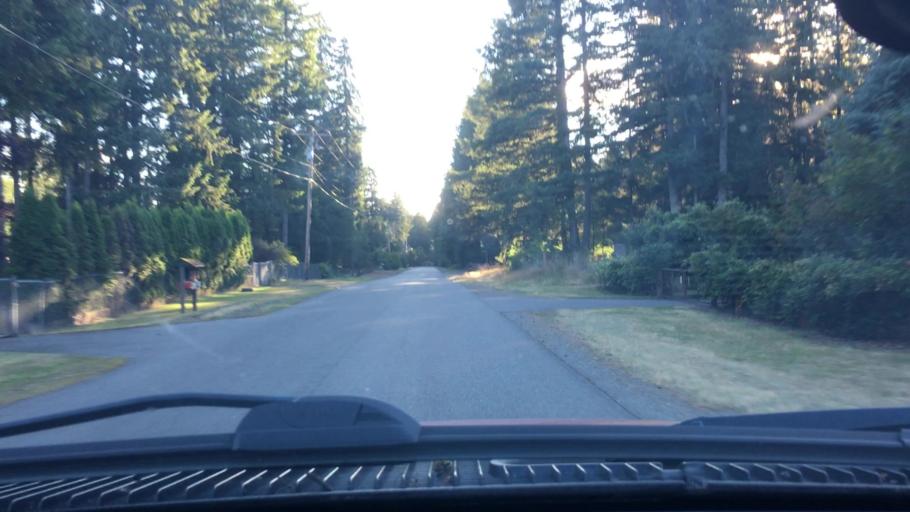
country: US
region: Washington
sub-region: King County
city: Lake Morton-Berrydale
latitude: 47.3473
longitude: -122.0754
